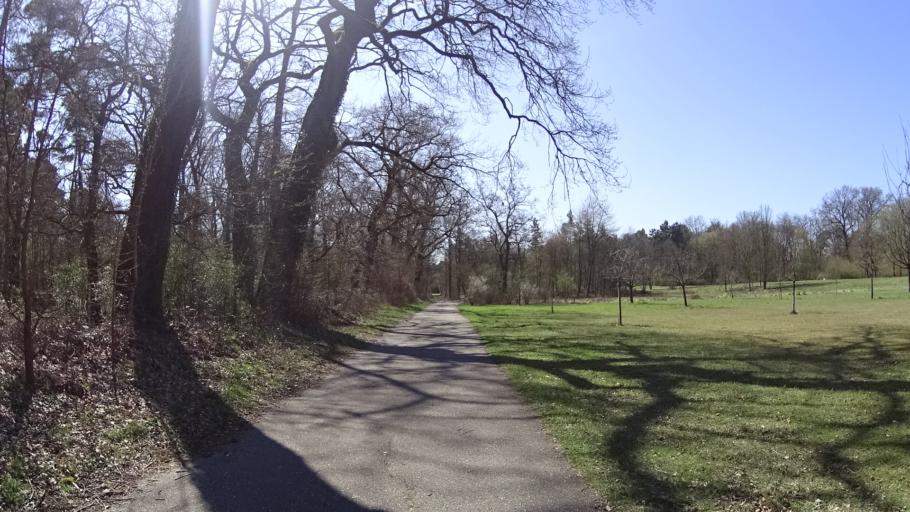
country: DE
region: Baden-Wuerttemberg
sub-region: Karlsruhe Region
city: Bruhl
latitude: 49.4272
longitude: 8.5473
